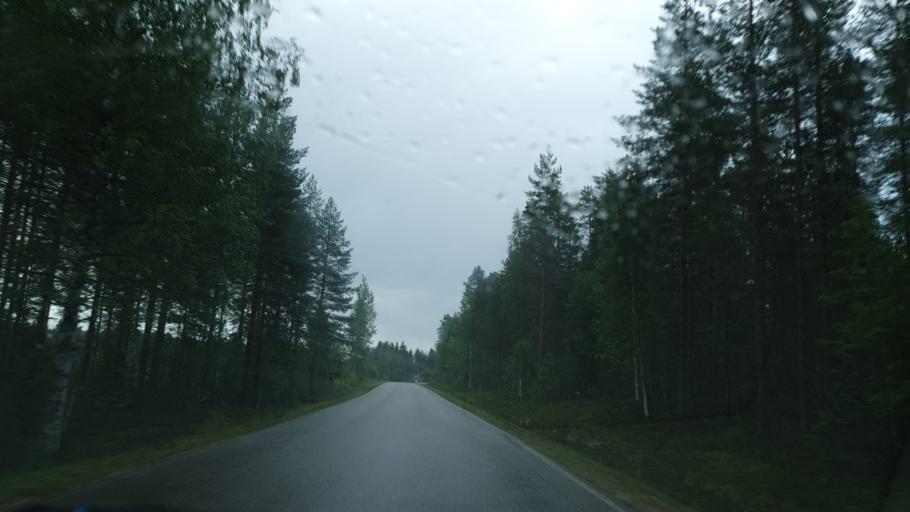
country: FI
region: Kainuu
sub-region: Kehys-Kainuu
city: Kuhmo
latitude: 64.1700
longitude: 29.3679
